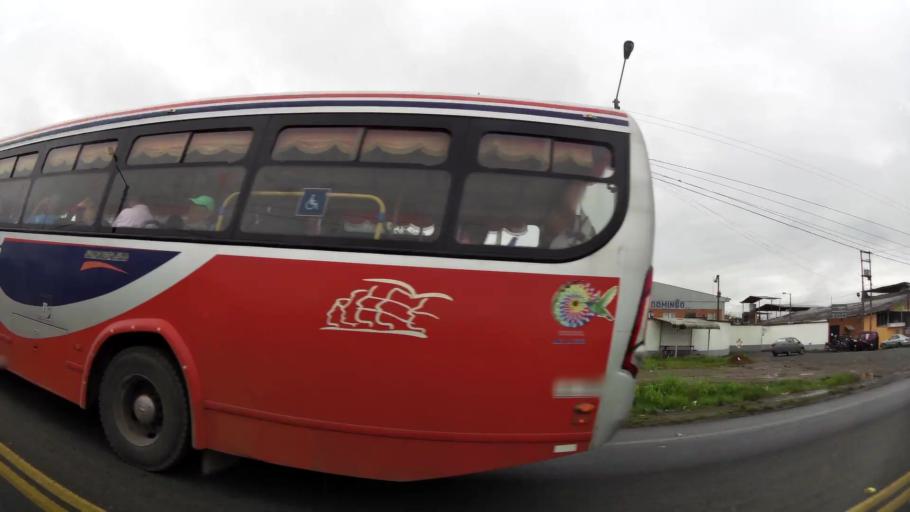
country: EC
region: Santo Domingo de los Tsachilas
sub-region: Canton Santo Domingo de los Colorados
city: Santo Domingo de los Colorados
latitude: -0.2423
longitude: -79.1941
